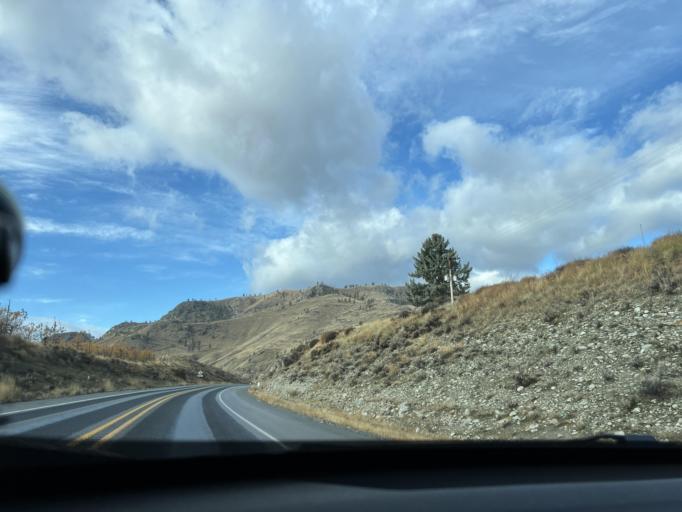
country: US
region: Washington
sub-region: Chelan County
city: Chelan
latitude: 47.8622
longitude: -119.9413
